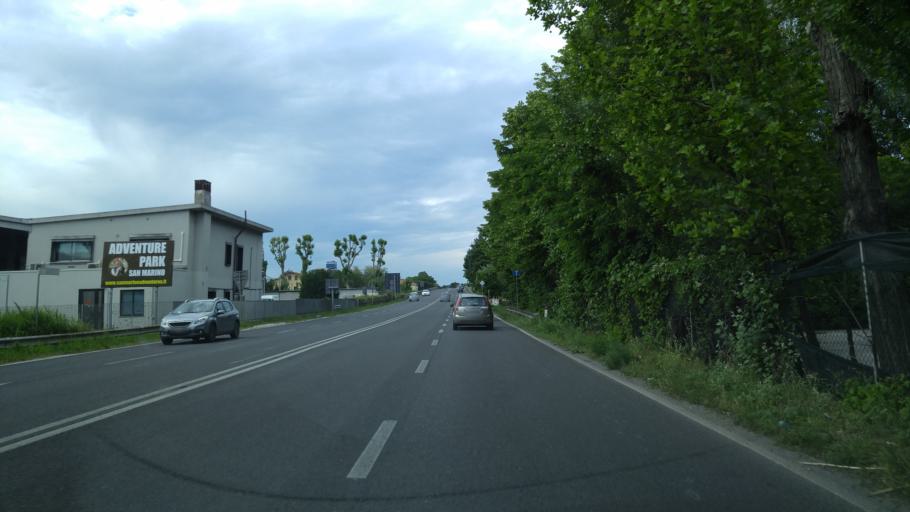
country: IT
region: Emilia-Romagna
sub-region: Provincia di Rimini
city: Rimini
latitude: 44.0654
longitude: 12.5415
